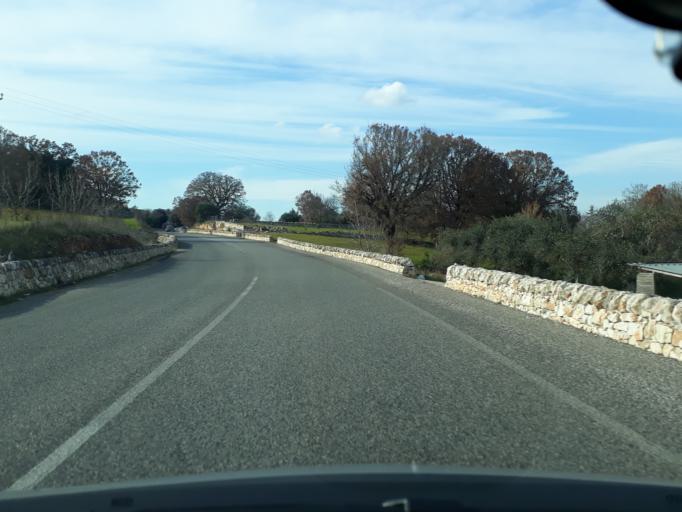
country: IT
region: Apulia
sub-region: Provincia di Bari
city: Locorotondo
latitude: 40.7604
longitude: 17.3374
